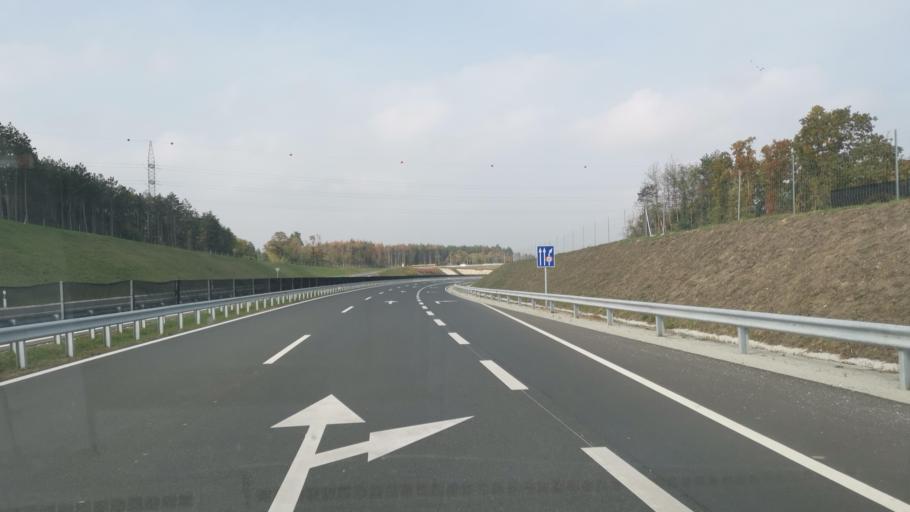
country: HU
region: Gyor-Moson-Sopron
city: Sopron
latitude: 47.6747
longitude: 16.6286
